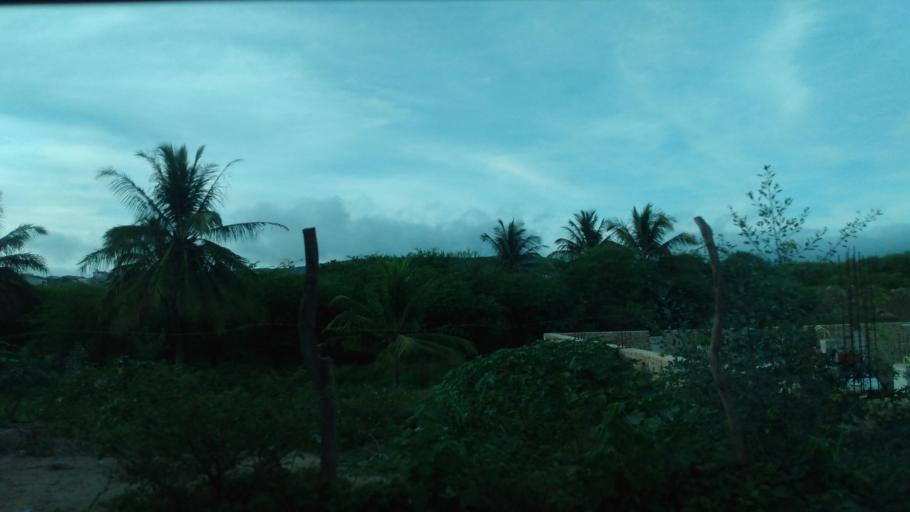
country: BR
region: Pernambuco
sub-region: Bezerros
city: Bezerros
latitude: -8.2245
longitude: -35.7502
